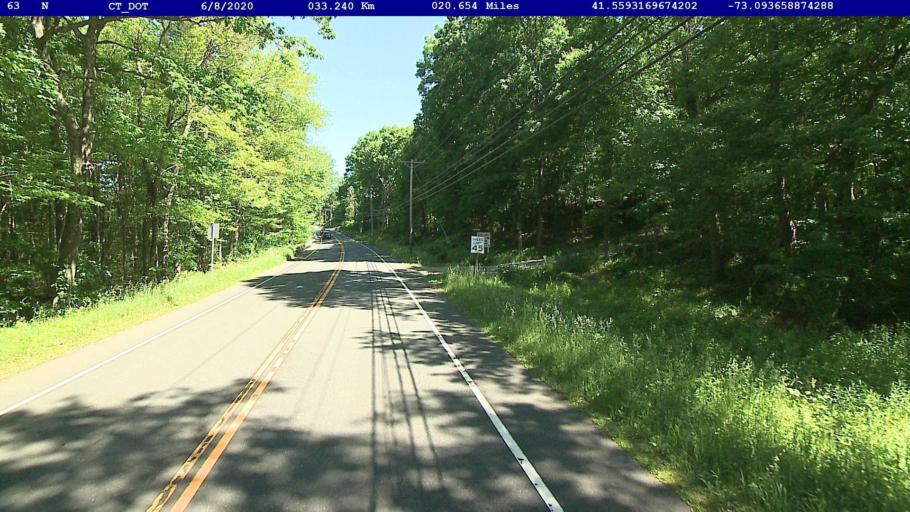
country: US
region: Connecticut
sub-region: Litchfield County
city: Oakville
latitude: 41.5593
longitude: -73.0937
